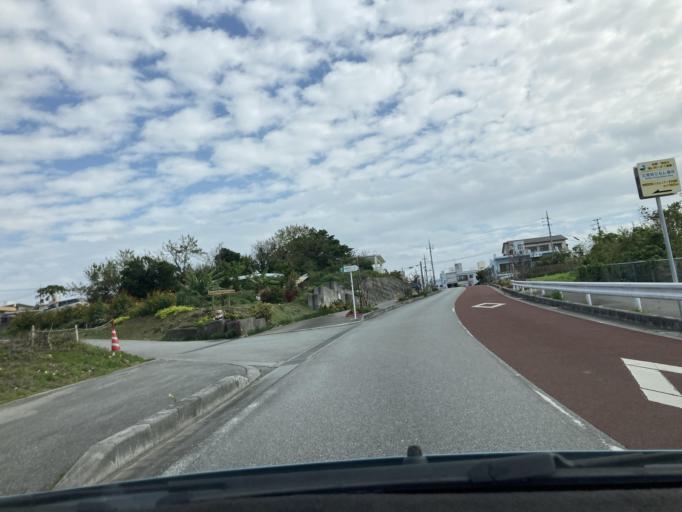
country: JP
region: Okinawa
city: Tomigusuku
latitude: 26.1861
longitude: 127.6919
